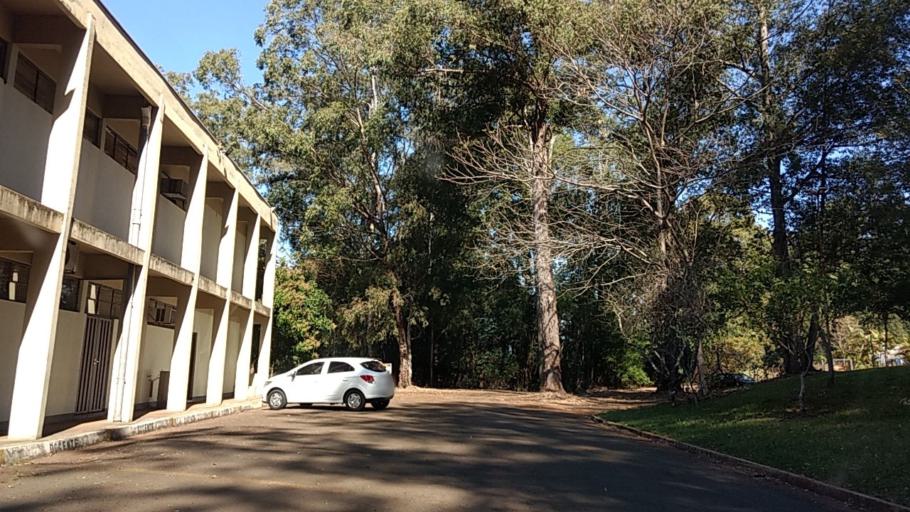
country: BR
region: Sao Paulo
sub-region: Botucatu
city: Botucatu
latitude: -22.8550
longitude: -48.4329
